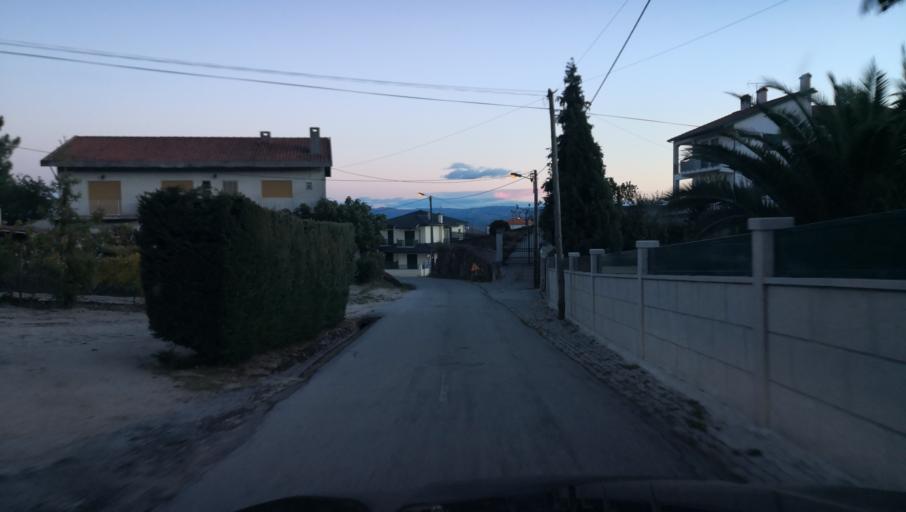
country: PT
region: Vila Real
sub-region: Santa Marta de Penaguiao
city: Santa Marta de Penaguiao
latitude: 41.2604
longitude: -7.7835
